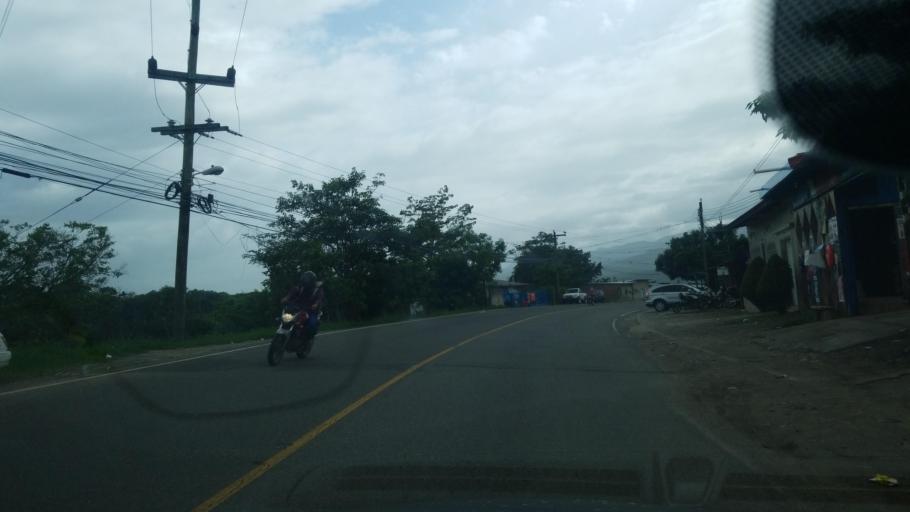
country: HN
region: Ocotepeque
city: Sinuapa
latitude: 14.4432
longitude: -89.1775
